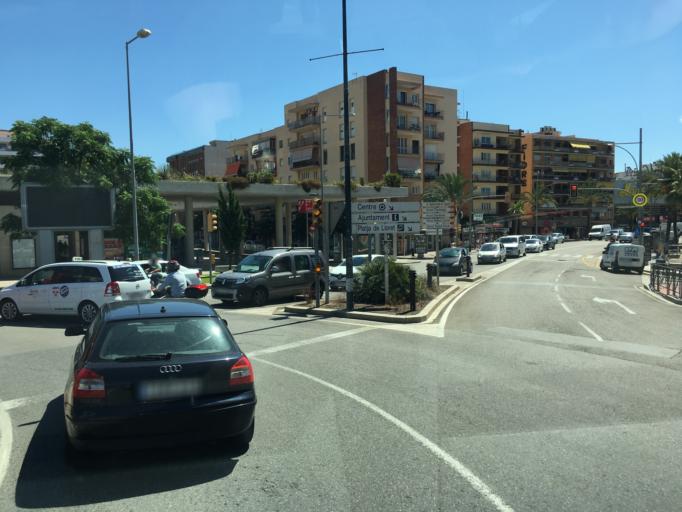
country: ES
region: Catalonia
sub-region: Provincia de Girona
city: Lloret de Mar
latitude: 41.7006
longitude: 2.8415
